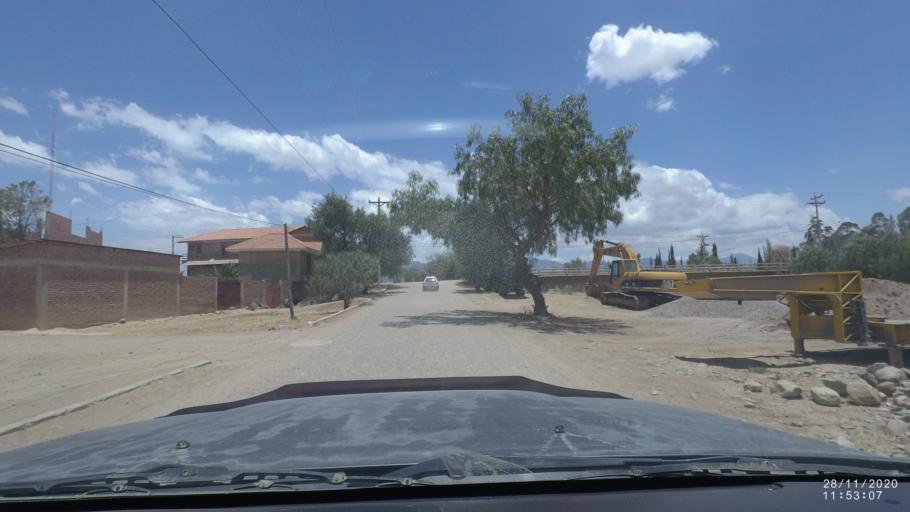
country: BO
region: Cochabamba
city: Tarata
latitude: -17.6113
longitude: -66.0212
